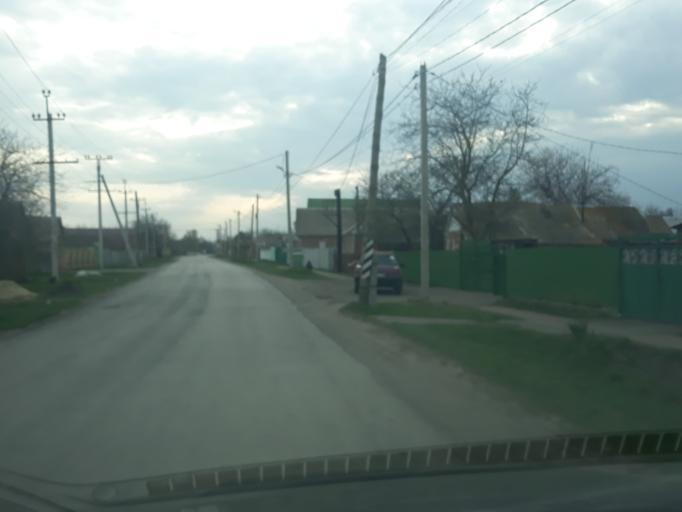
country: RU
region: Rostov
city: Novobessergenovka
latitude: 47.1604
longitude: 38.7148
